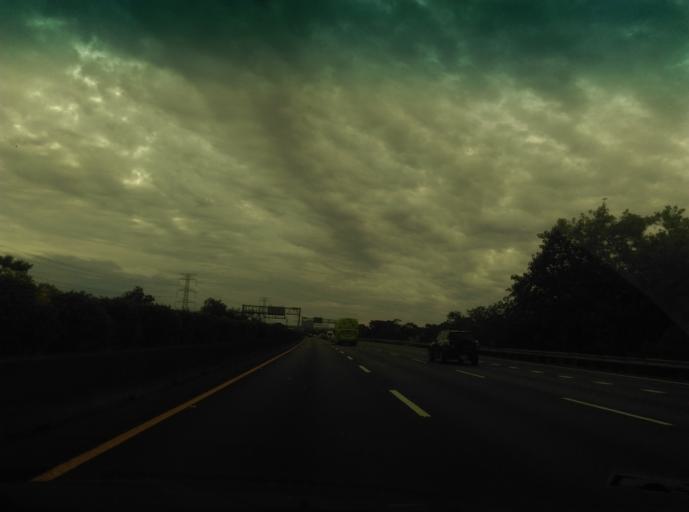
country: TW
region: Taiwan
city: Daxi
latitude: 24.9337
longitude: 121.3154
